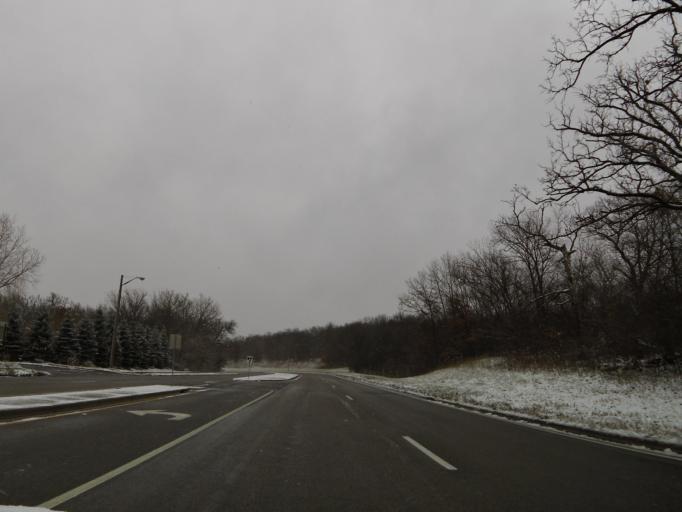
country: US
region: Minnesota
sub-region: Scott County
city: Prior Lake
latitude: 44.7582
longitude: -93.4042
